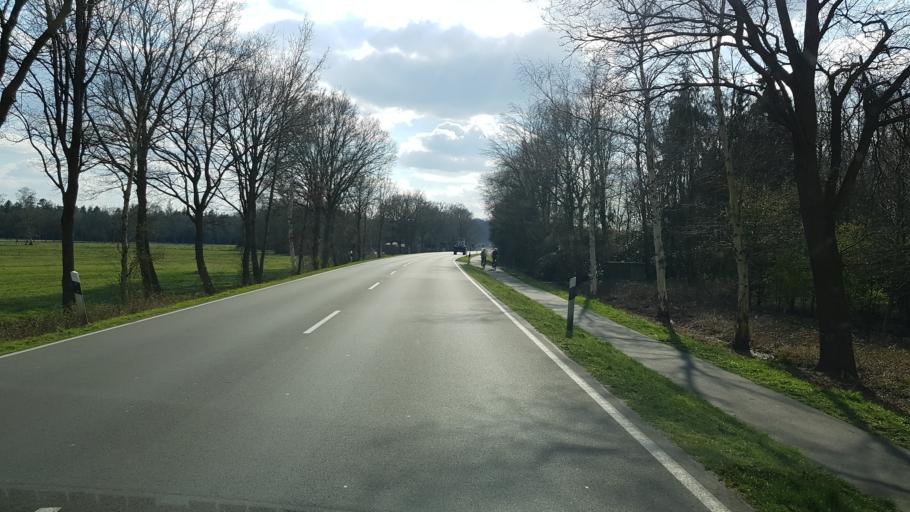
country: DE
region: Lower Saxony
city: Rastede
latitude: 53.2374
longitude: 8.2816
